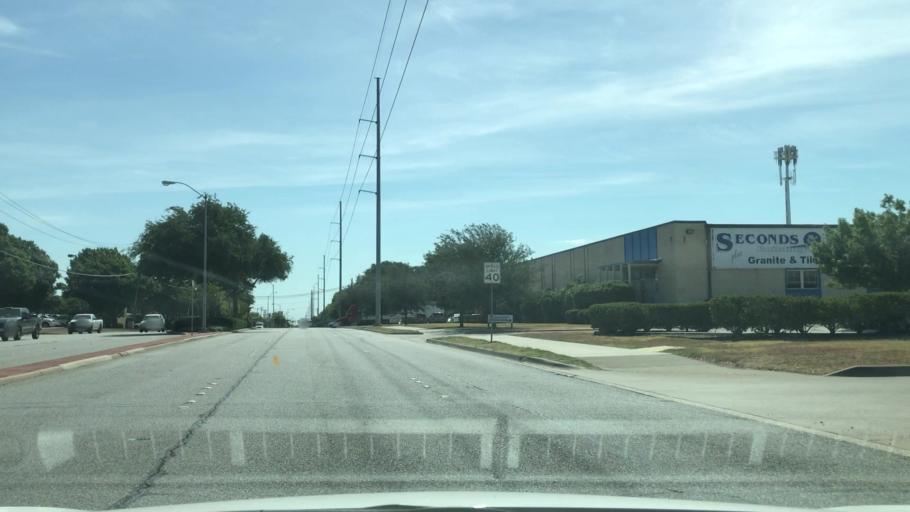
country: US
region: Texas
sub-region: Dallas County
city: Richardson
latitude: 32.9607
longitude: -96.7240
